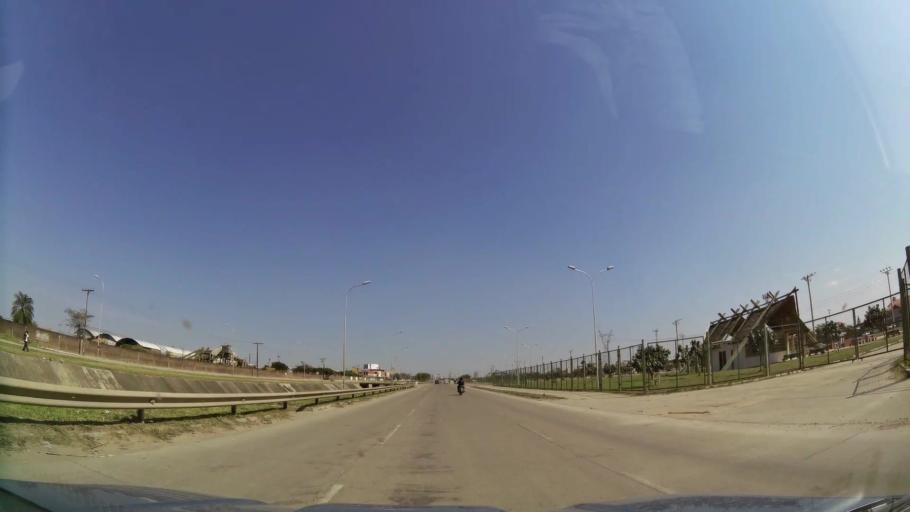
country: BO
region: Santa Cruz
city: Santa Cruz de la Sierra
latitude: -17.7398
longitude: -63.1432
